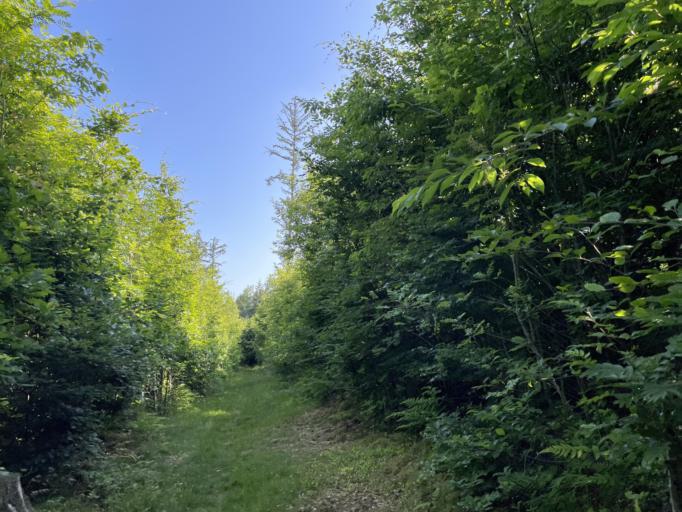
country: DE
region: Schleswig-Holstein
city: Mildstedt
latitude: 54.4717
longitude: 9.1036
